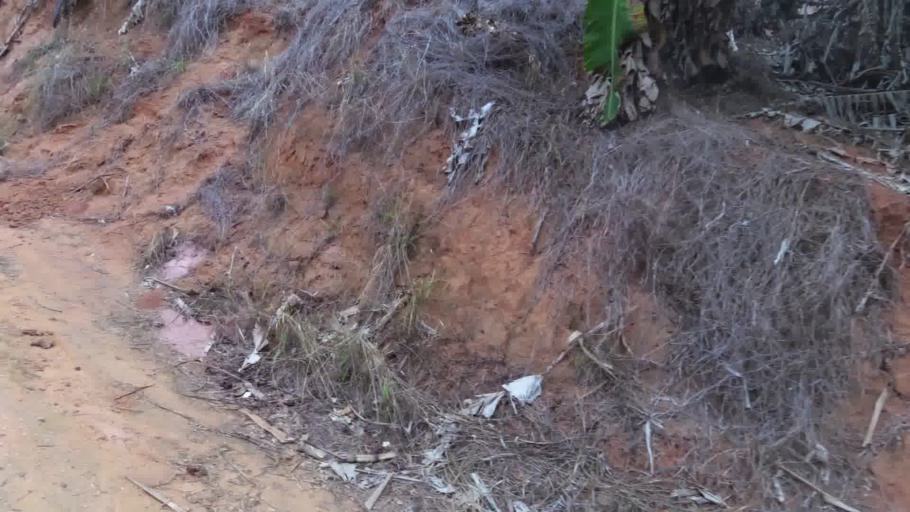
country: BR
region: Espirito Santo
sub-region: Alfredo Chaves
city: Alfredo Chaves
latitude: -20.6387
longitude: -40.7557
